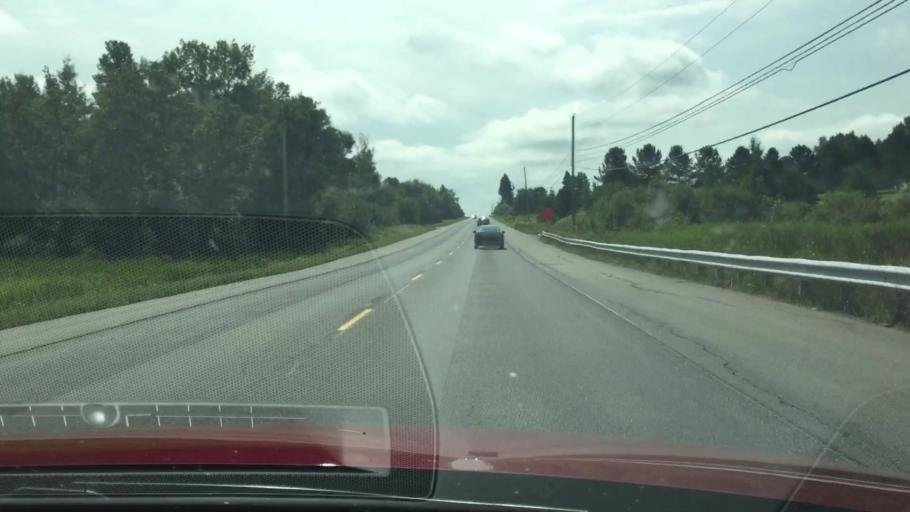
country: US
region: Maine
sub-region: Aroostook County
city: Houlton
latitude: 46.3482
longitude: -67.8420
